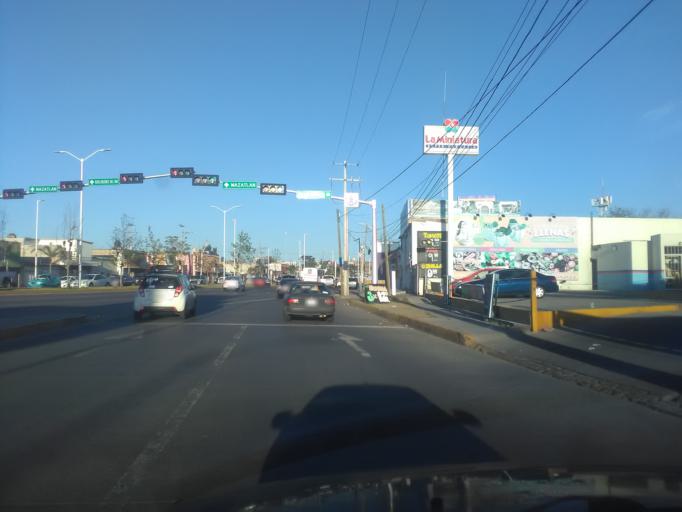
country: MX
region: Durango
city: Victoria de Durango
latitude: 24.0364
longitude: -104.6781
